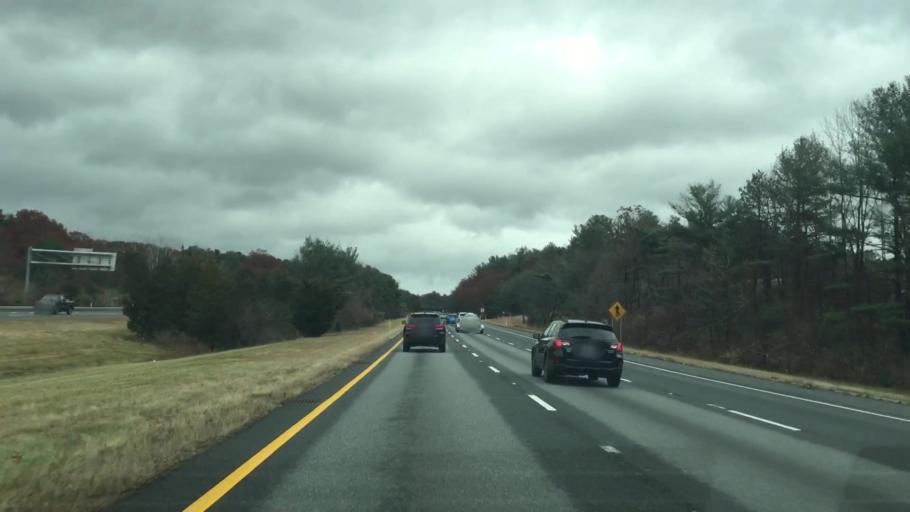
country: US
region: Massachusetts
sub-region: Essex County
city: Merrimac
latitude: 42.8301
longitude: -70.9921
